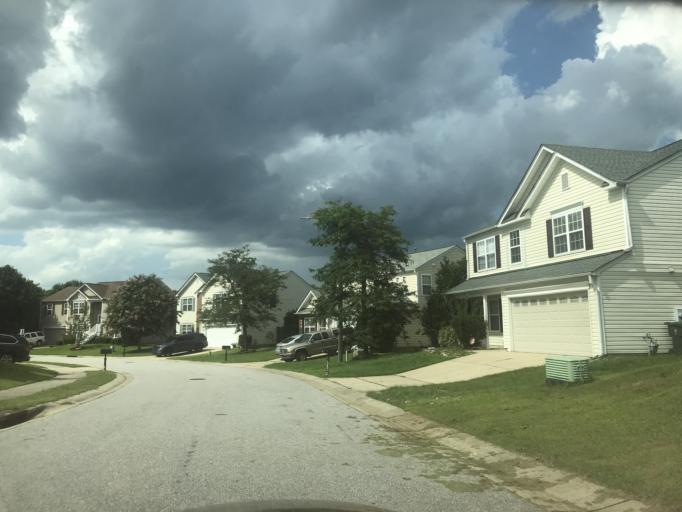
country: US
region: North Carolina
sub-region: Wake County
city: Knightdale
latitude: 35.8413
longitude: -78.5585
